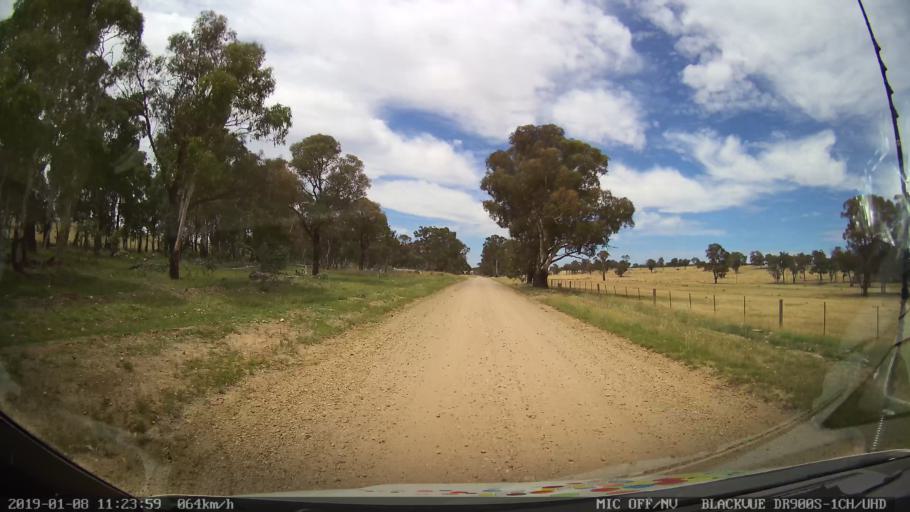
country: AU
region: New South Wales
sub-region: Guyra
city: Guyra
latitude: -30.2603
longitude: 151.5584
